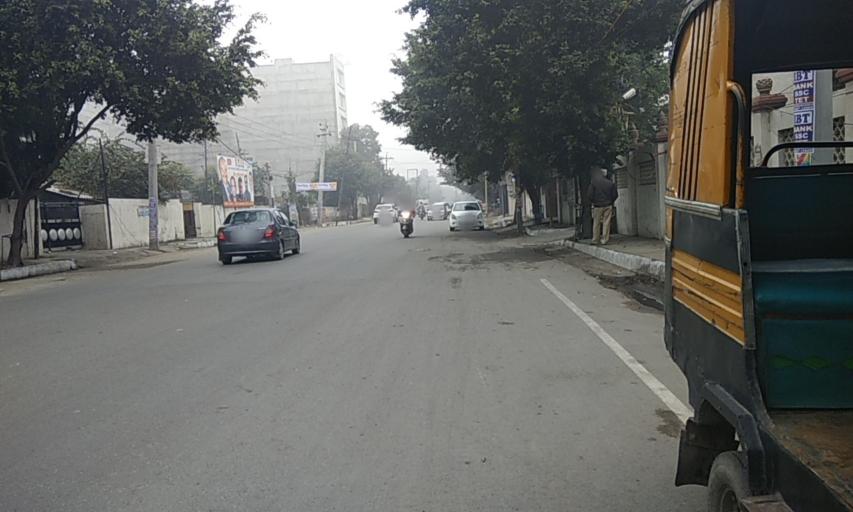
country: IN
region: Punjab
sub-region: Amritsar
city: Amritsar
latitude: 31.6393
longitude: 74.8664
